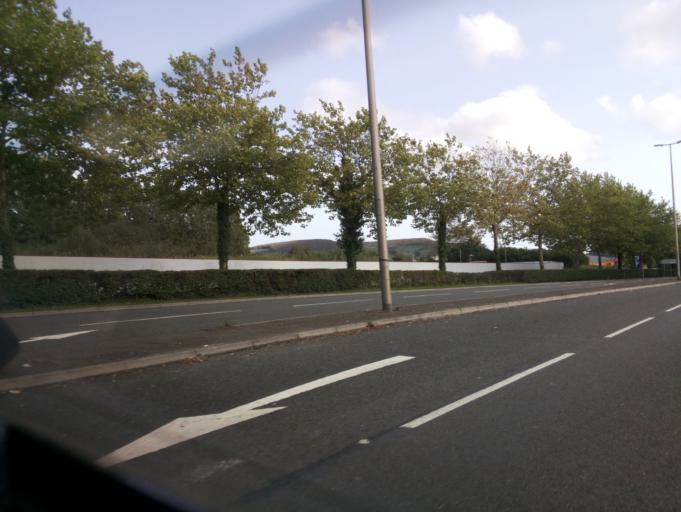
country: GB
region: Wales
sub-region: Caerphilly County Borough
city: Abertridwr
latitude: 51.5718
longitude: -3.2882
